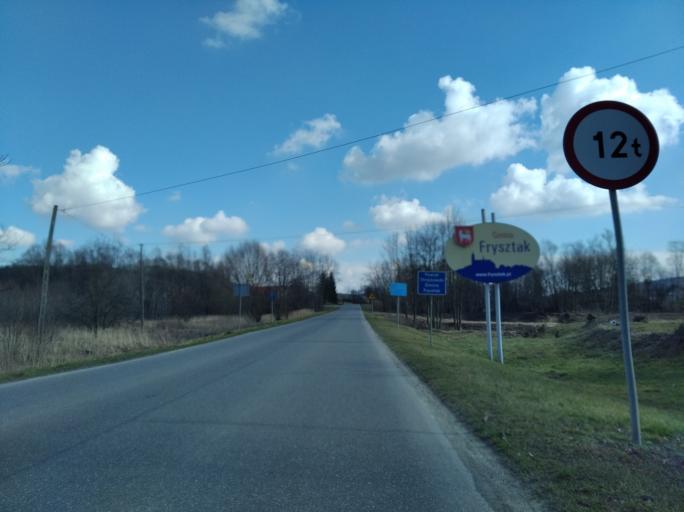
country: PL
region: Subcarpathian Voivodeship
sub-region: Powiat jasielski
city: Kolaczyce
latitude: 49.8591
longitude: 21.4816
